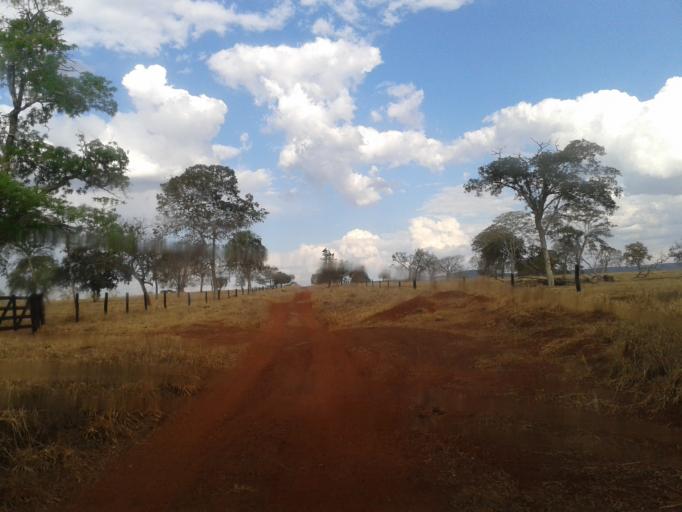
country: BR
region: Minas Gerais
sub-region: Santa Vitoria
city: Santa Vitoria
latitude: -19.1762
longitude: -49.9865
